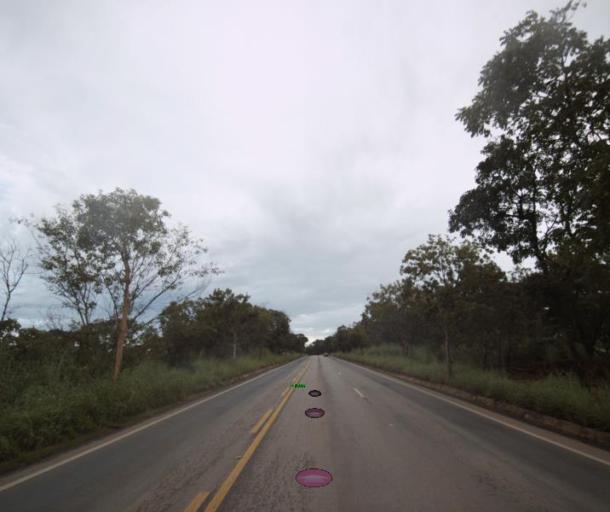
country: BR
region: Goias
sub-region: Porangatu
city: Porangatu
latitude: -13.7401
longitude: -49.0295
